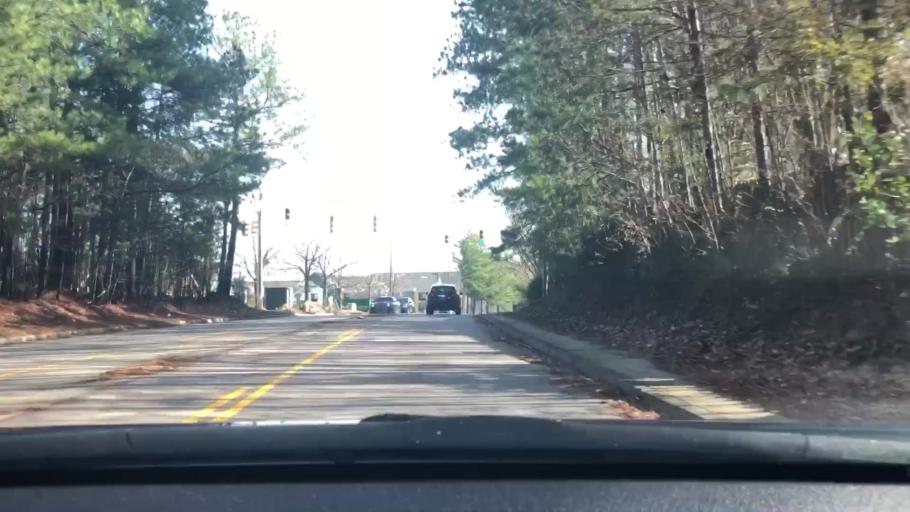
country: US
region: South Carolina
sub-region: Lexington County
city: Irmo
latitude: 34.0888
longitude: -81.1662
